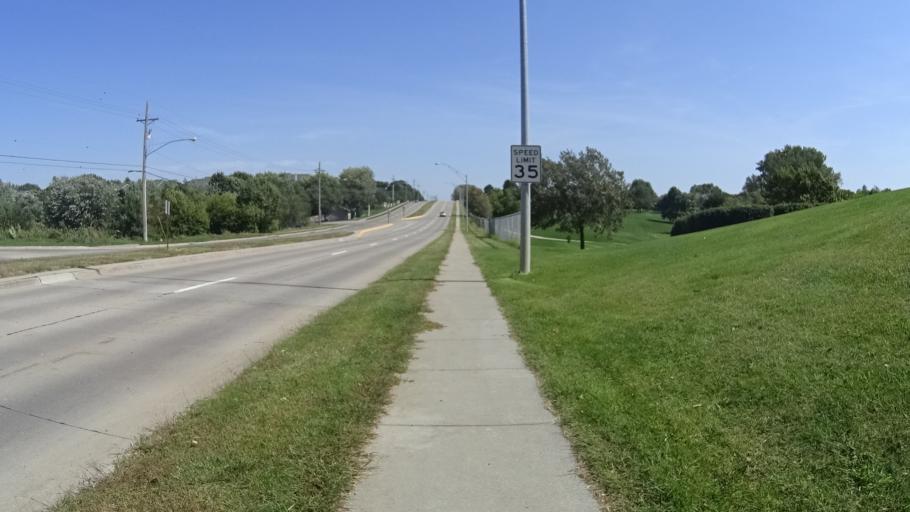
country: US
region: Nebraska
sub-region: Sarpy County
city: La Vista
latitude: 41.1761
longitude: -96.0533
